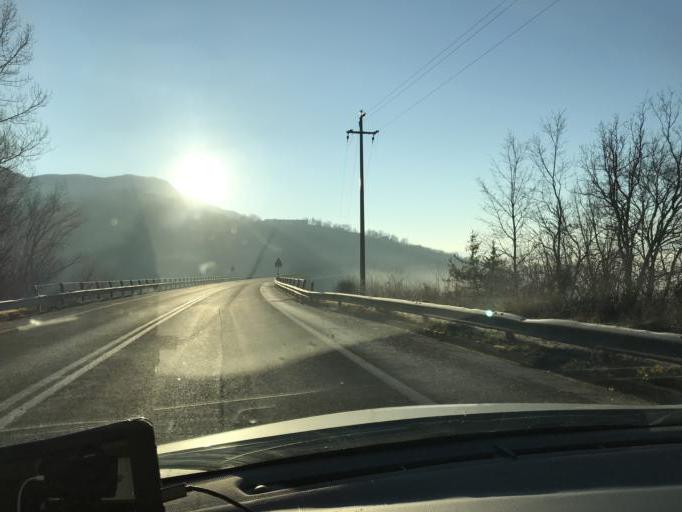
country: IT
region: Latium
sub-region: Provincia di Rieti
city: Petrella Salto
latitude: 42.2962
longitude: 13.0587
